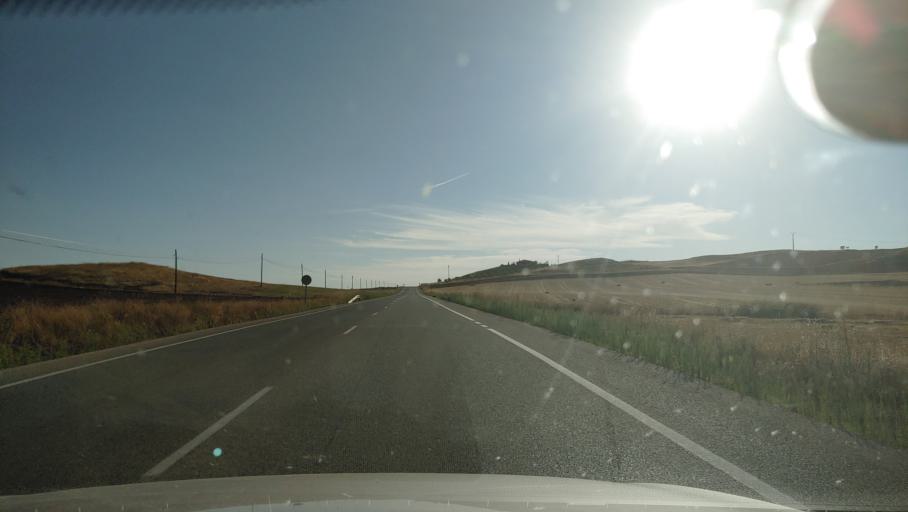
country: ES
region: Castille-La Mancha
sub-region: Provincia de Ciudad Real
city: Fuenllana
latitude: 38.7478
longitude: -2.9732
